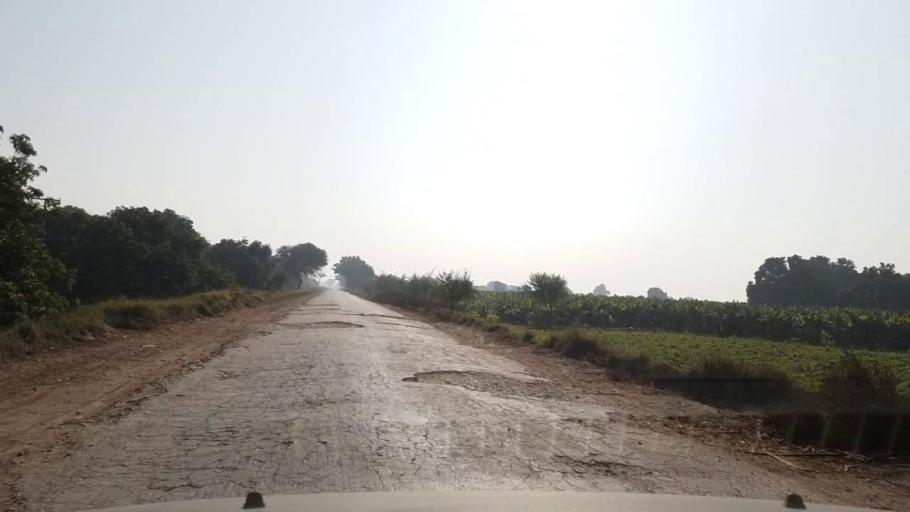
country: PK
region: Sindh
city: Matiari
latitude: 25.5555
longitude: 68.5355
